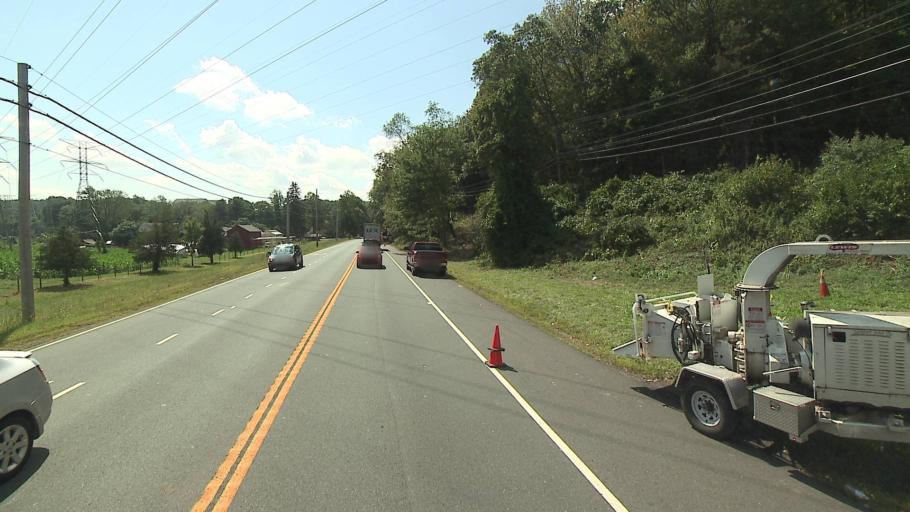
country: US
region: Connecticut
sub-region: Fairfield County
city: Shelton
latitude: 41.2801
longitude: -73.1191
